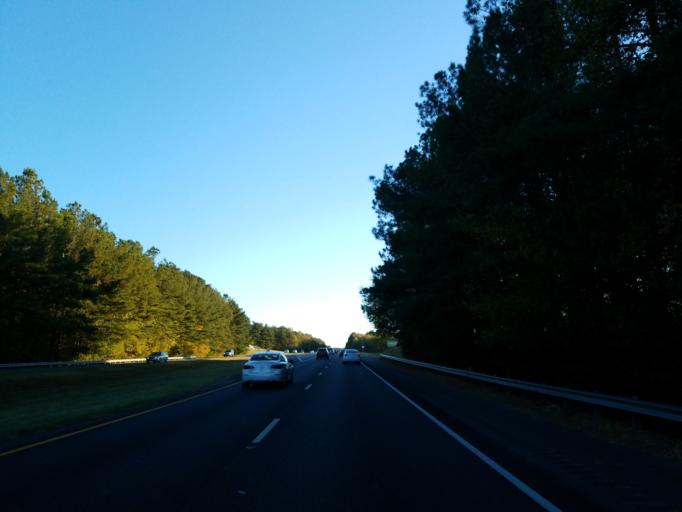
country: US
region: Georgia
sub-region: Forsyth County
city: Cumming
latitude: 34.2953
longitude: -84.0742
